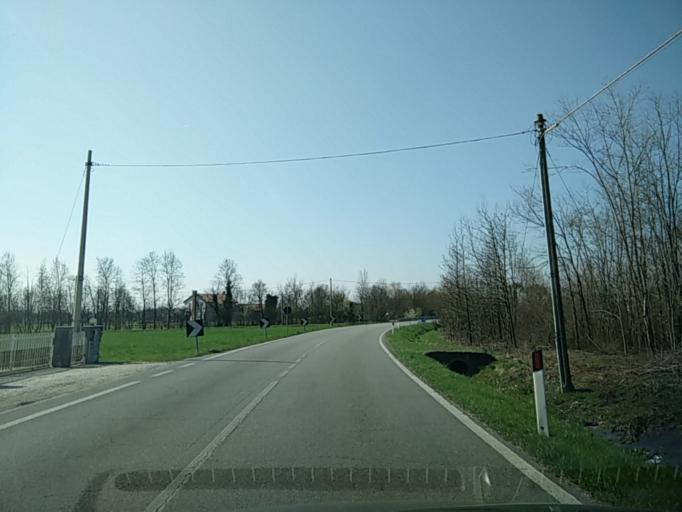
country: IT
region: Veneto
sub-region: Provincia di Treviso
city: Valla
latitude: 45.7018
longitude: 11.9089
